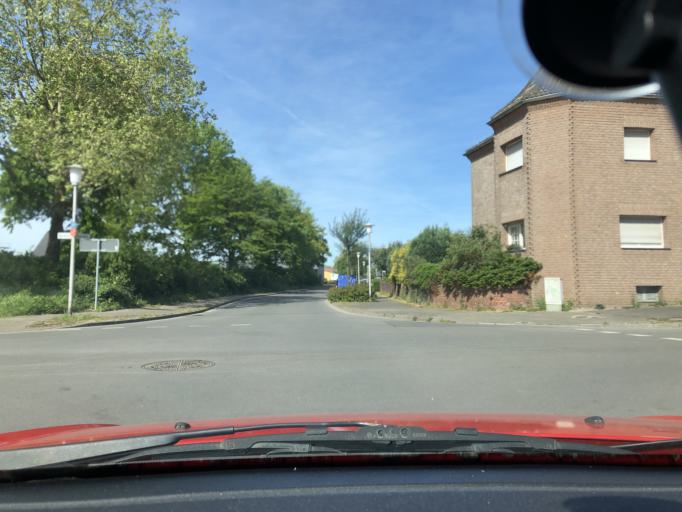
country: DE
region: North Rhine-Westphalia
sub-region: Regierungsbezirk Dusseldorf
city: Kamp-Lintfort
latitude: 51.5020
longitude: 6.5392
